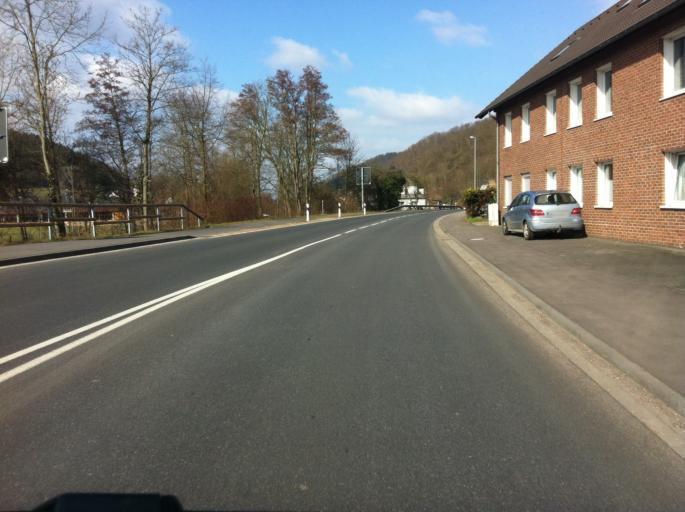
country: DE
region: North Rhine-Westphalia
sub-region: Regierungsbezirk Koln
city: Bad Munstereifel
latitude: 50.5340
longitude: 6.7695
